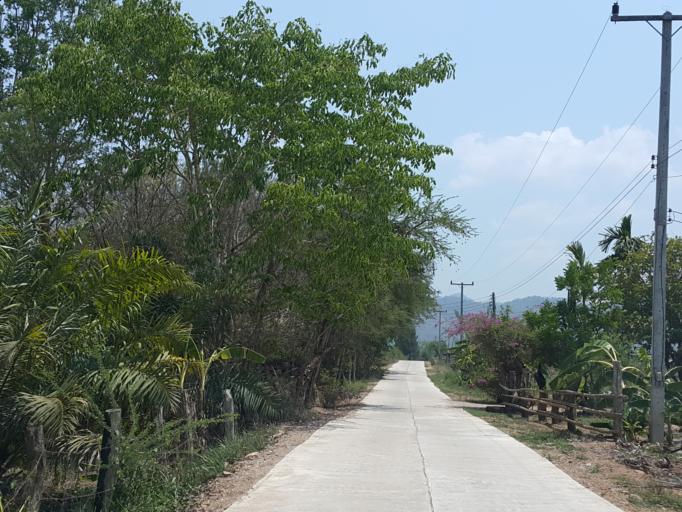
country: TH
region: Kanchanaburi
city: Sai Yok
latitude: 14.1710
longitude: 98.9587
